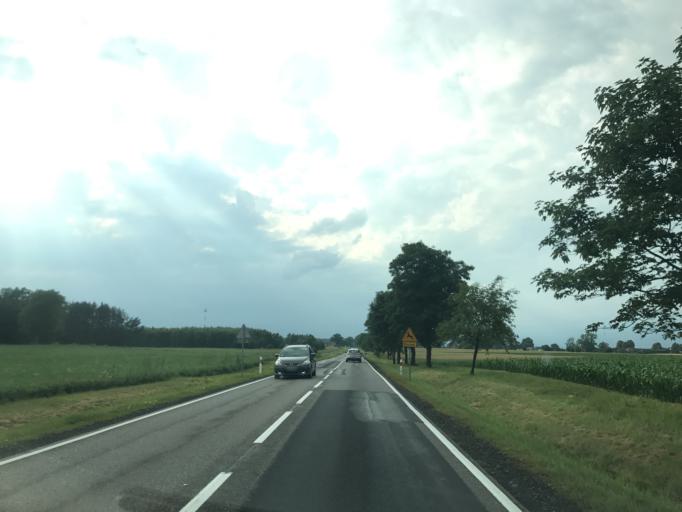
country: PL
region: Pomeranian Voivodeship
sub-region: Powiat czluchowski
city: Przechlewo
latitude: 53.7043
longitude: 17.2687
